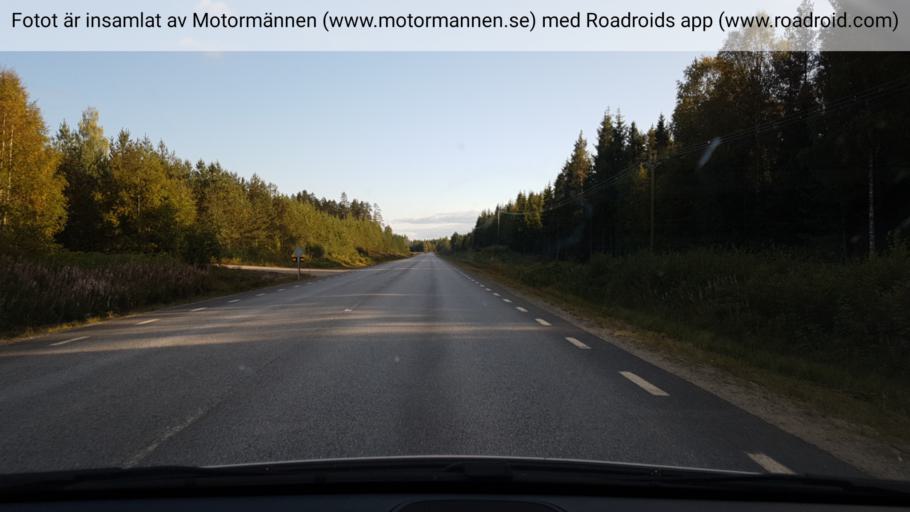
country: SE
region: Vaesterbotten
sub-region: Vannas Kommun
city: Vaennaes
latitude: 64.0188
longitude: 19.6923
